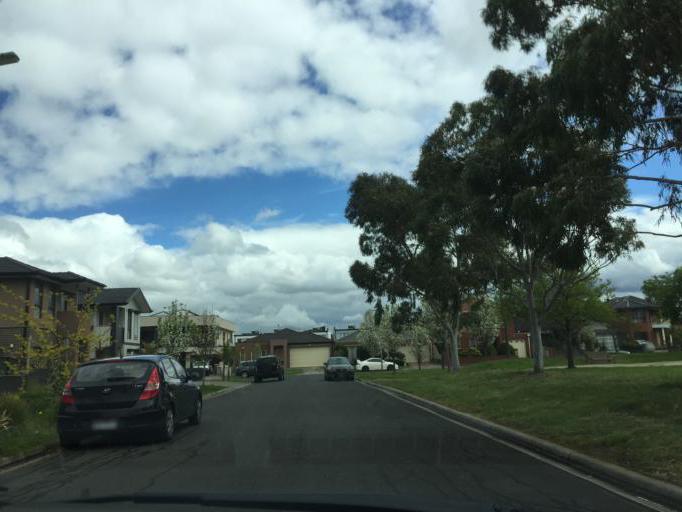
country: AU
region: Victoria
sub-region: Maribyrnong
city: Braybrook
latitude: -37.7950
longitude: 144.8519
